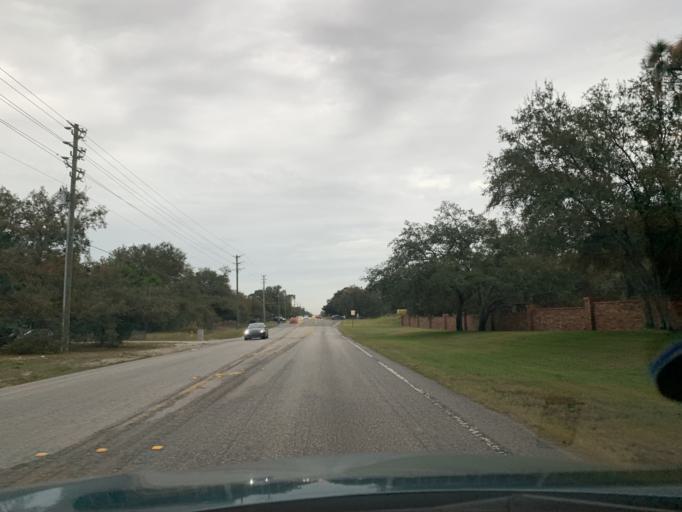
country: US
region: Florida
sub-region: Hernando County
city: Timber Pines
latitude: 28.4339
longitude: -82.5845
